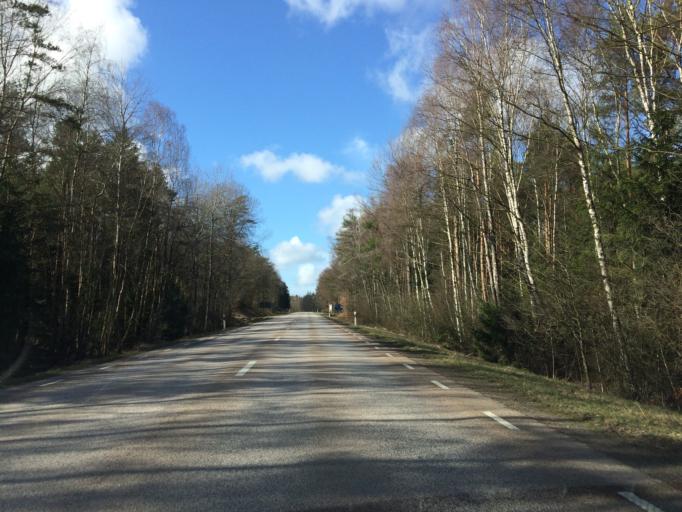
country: SE
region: Kronoberg
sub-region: Markaryds Kommun
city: Markaryd
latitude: 56.4936
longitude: 13.4574
